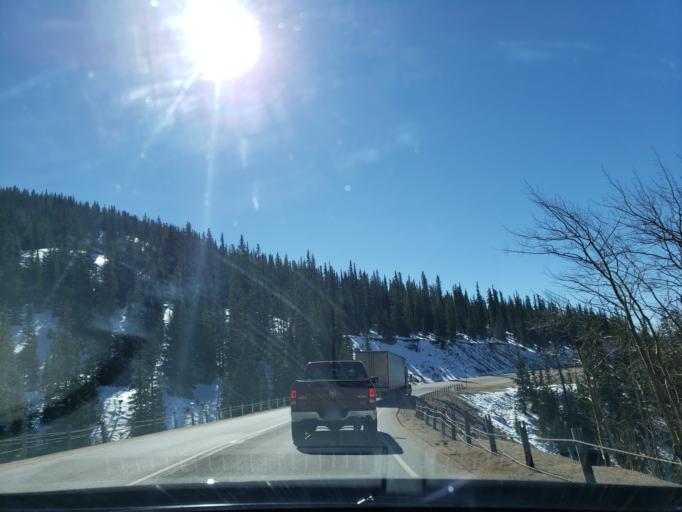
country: US
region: Colorado
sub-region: Park County
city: Fairplay
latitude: 39.3448
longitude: -106.0524
